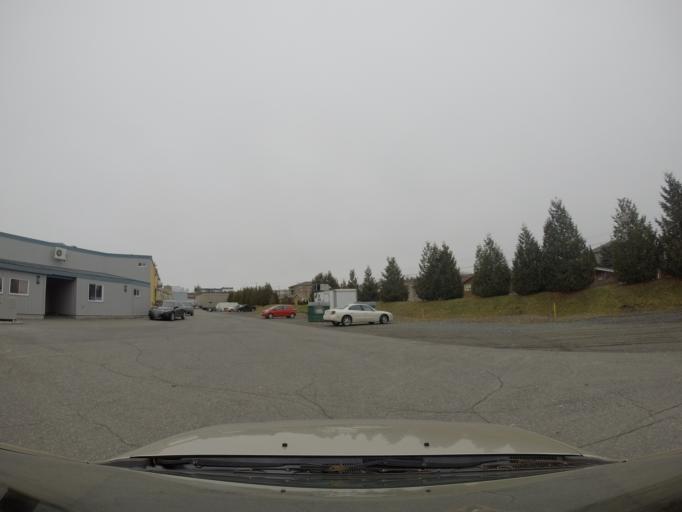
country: CA
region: Ontario
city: Greater Sudbury
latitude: 46.4629
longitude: -81.0292
